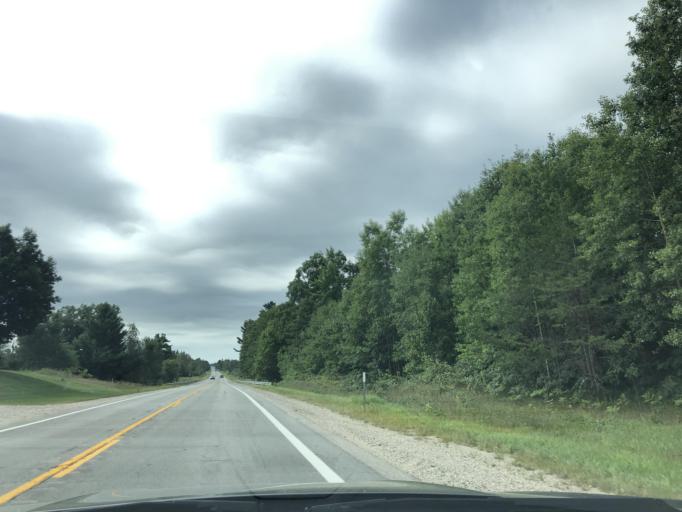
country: US
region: Michigan
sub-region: Missaukee County
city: Lake City
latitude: 44.2569
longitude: -85.2153
